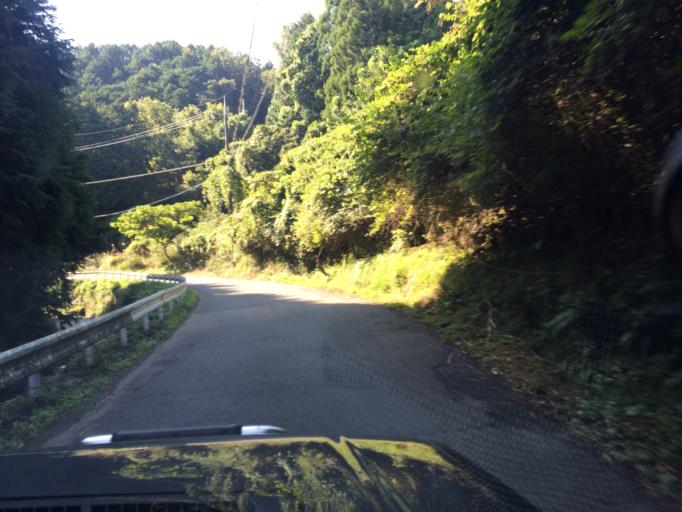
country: JP
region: Nara
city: Nara-shi
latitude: 34.7426
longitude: 135.9500
